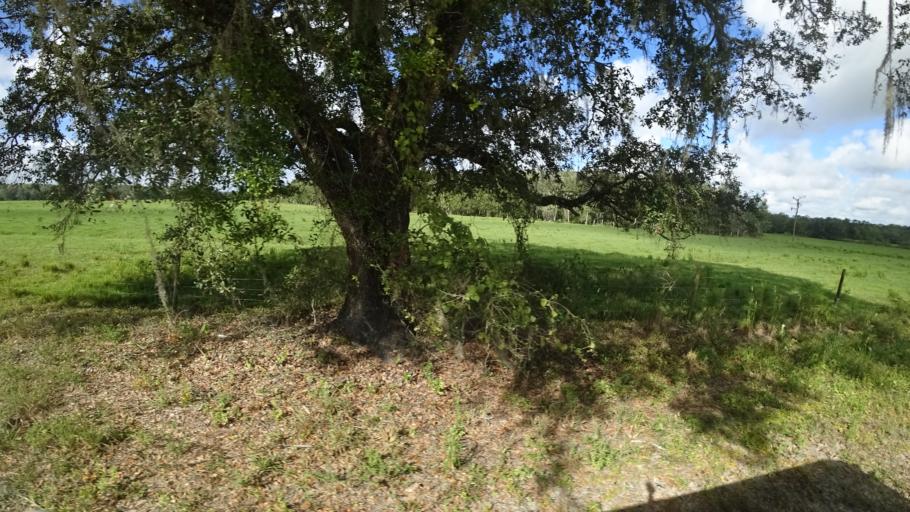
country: US
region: Florida
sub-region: Sarasota County
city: Lake Sarasota
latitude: 27.3337
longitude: -82.2040
